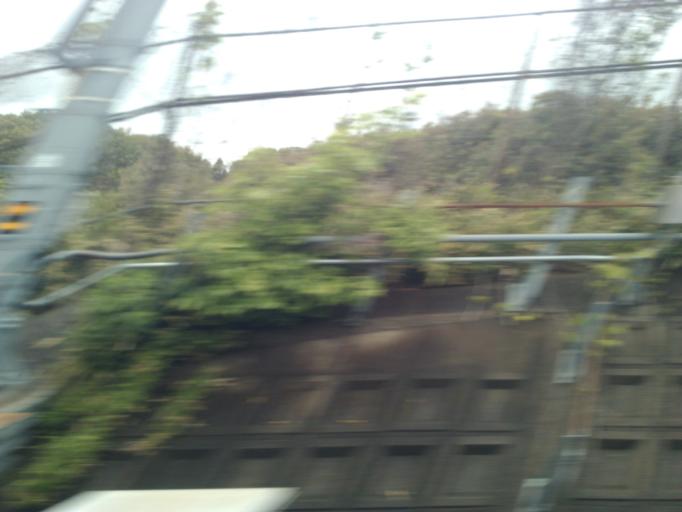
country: JP
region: Kanagawa
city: Yokohama
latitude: 35.4843
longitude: 139.5812
